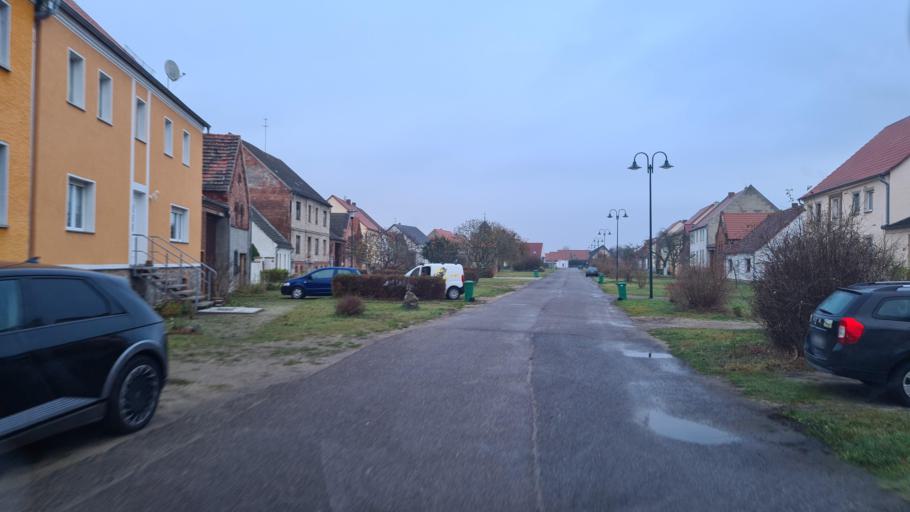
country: DE
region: Brandenburg
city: Beelitz
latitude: 52.1160
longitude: 13.0203
